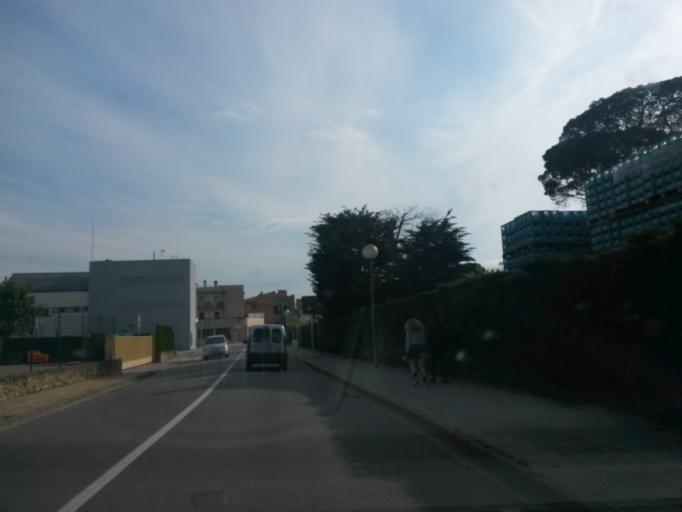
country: ES
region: Catalonia
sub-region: Provincia de Girona
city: Caldes de Malavella
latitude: 41.8384
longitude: 2.8072
